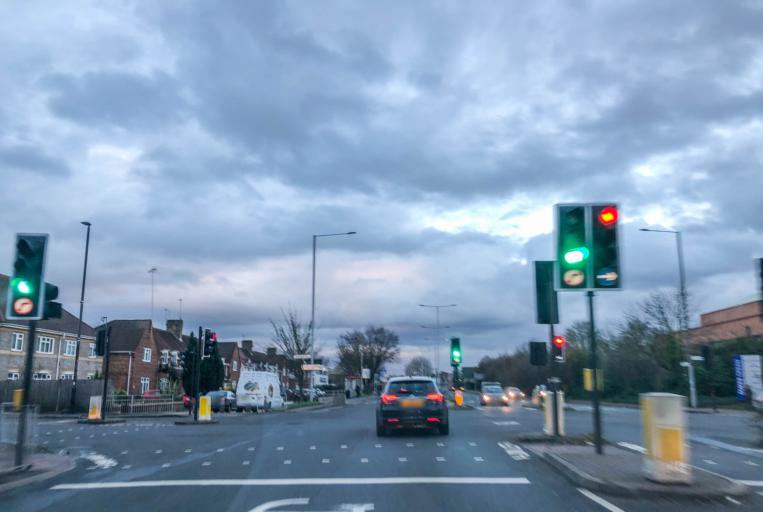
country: GB
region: England
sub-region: Greater London
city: Feltham
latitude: 51.4598
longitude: -0.4125
